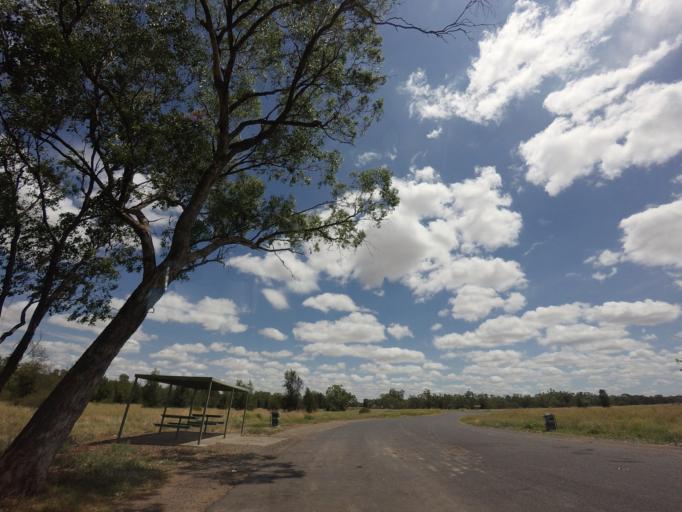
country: AU
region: New South Wales
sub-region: Moree Plains
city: Moree
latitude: -29.1825
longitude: 150.0093
